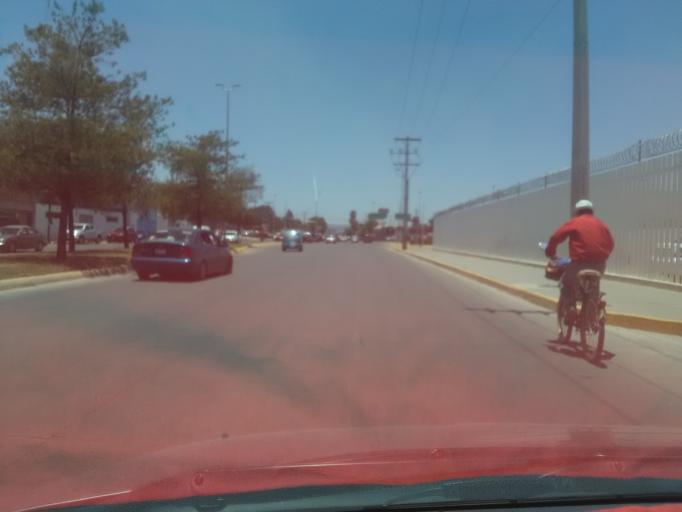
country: MX
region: Durango
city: Victoria de Durango
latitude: 24.0435
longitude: -104.6569
